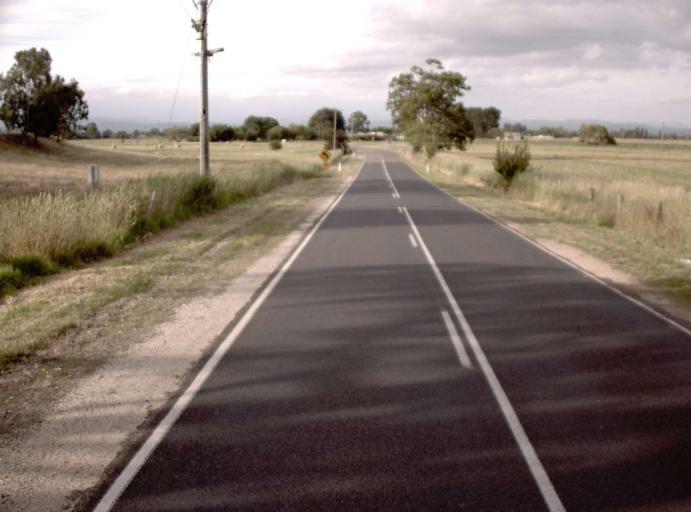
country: AU
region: Victoria
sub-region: Wellington
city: Sale
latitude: -37.9189
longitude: 146.9994
